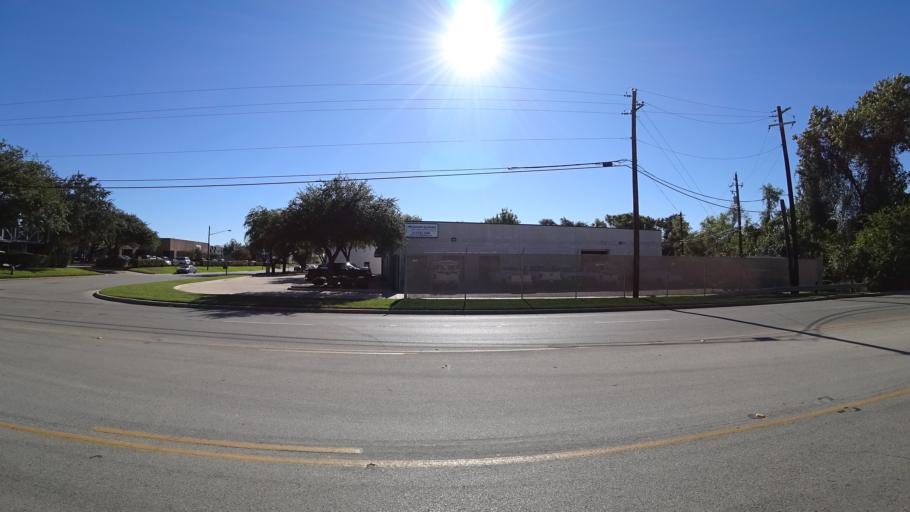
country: US
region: Texas
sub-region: Travis County
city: Manor
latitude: 30.3244
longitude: -97.6577
